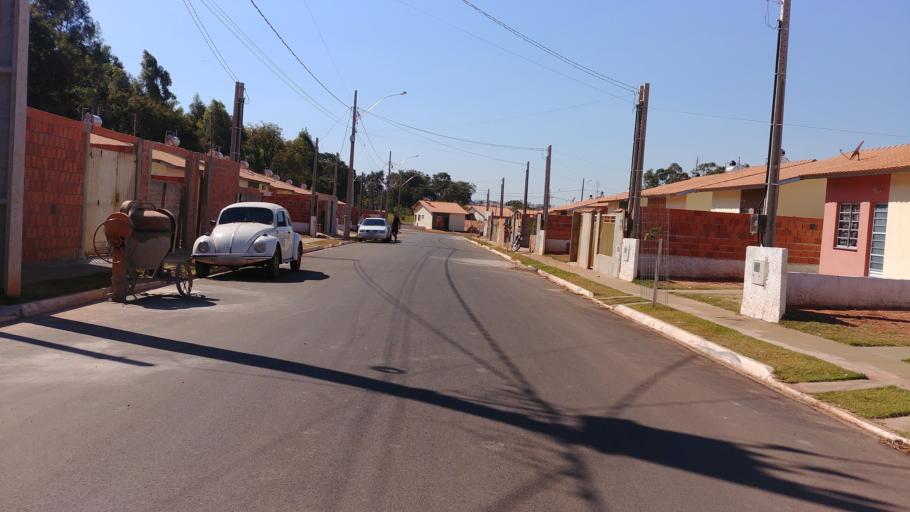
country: BR
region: Sao Paulo
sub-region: Paraguacu Paulista
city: Paraguacu Paulista
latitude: -22.4439
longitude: -50.5887
